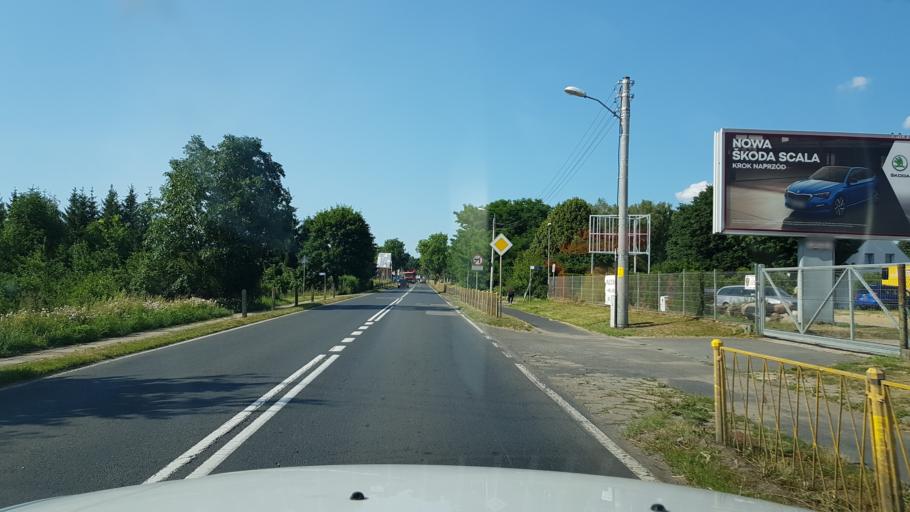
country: PL
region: West Pomeranian Voivodeship
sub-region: Powiat gryfinski
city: Stare Czarnowo
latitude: 53.3553
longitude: 14.7446
